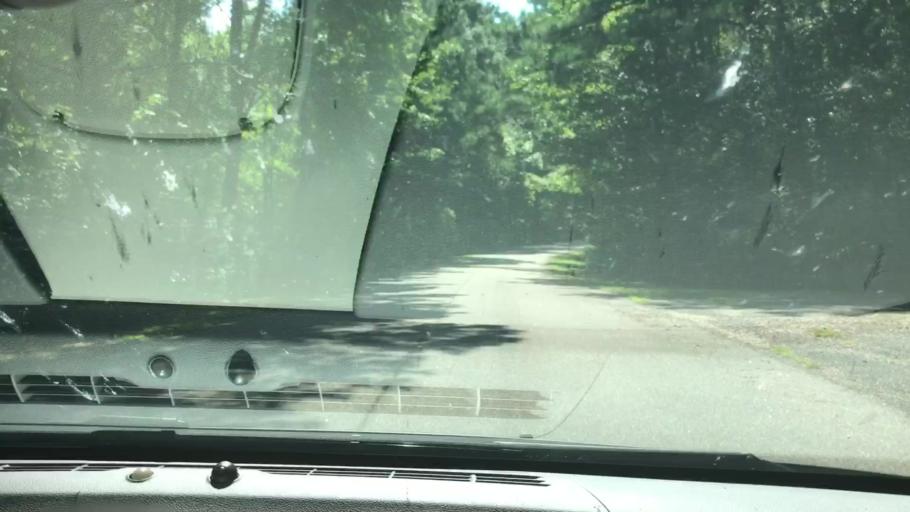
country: US
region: Georgia
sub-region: Troup County
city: La Grange
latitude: 33.0667
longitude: -85.1415
